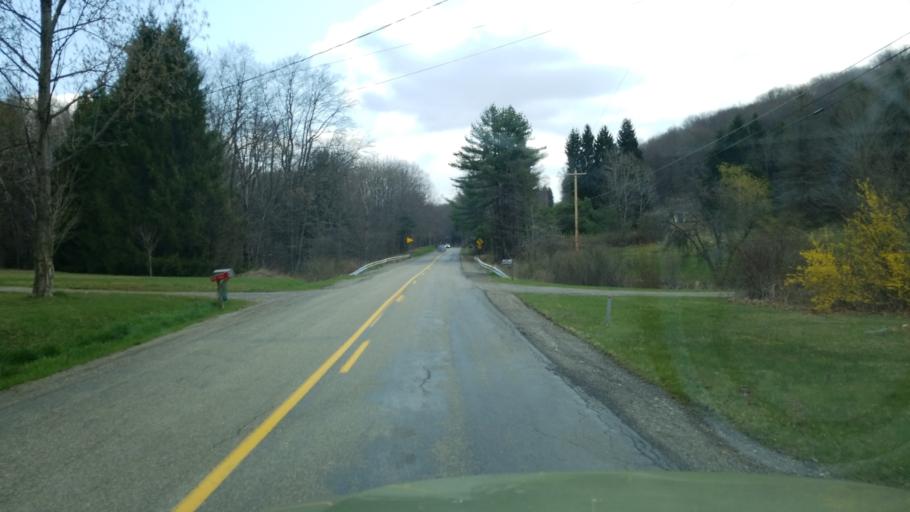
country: US
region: Pennsylvania
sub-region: Jefferson County
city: Brockway
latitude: 41.2727
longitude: -78.8283
